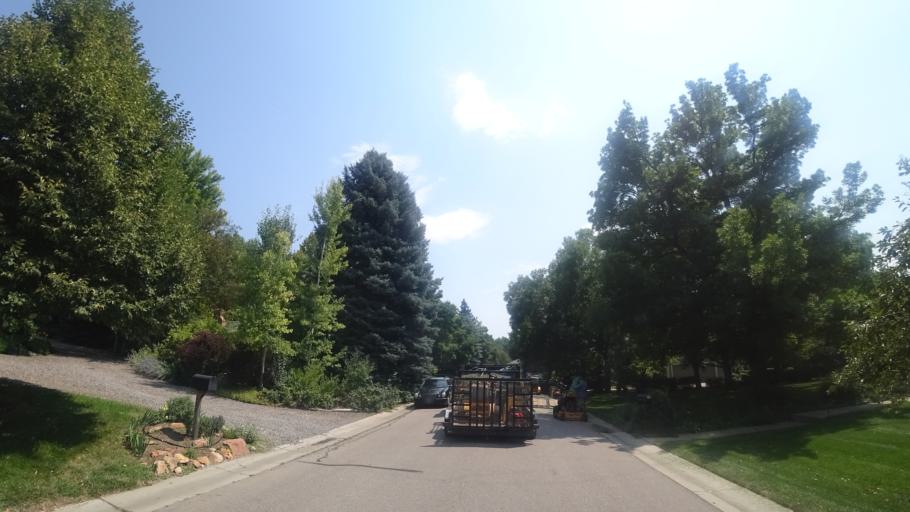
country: US
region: Colorado
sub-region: Arapahoe County
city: Greenwood Village
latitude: 39.6137
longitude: -104.9727
